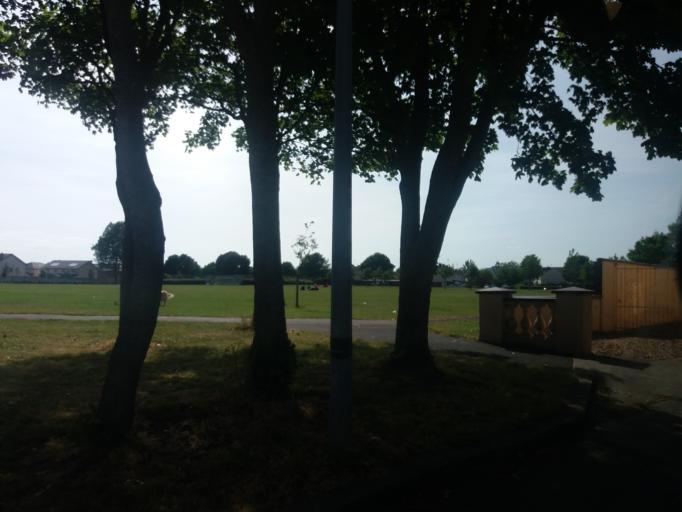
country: IE
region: Leinster
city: Lusk
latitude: 53.5219
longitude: -6.1619
